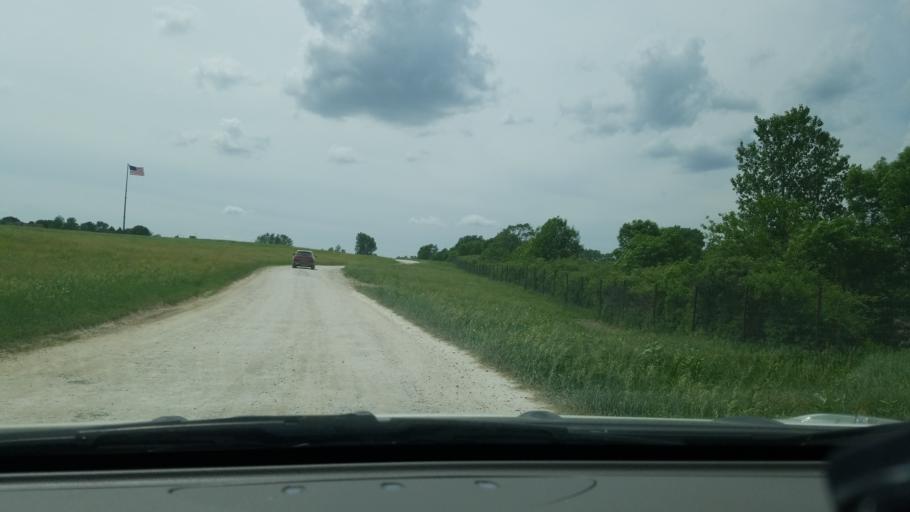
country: US
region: Nebraska
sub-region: Saunders County
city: Ashland
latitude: 41.0115
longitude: -96.2977
